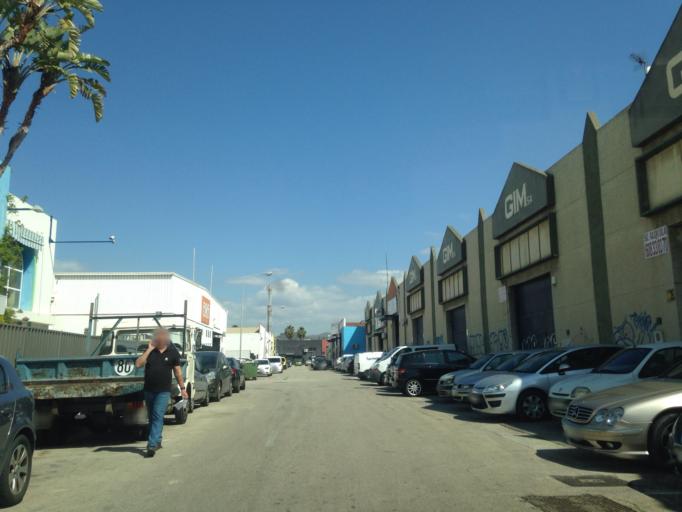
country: ES
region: Andalusia
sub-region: Provincia de Malaga
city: Malaga
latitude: 36.7025
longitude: -4.4746
